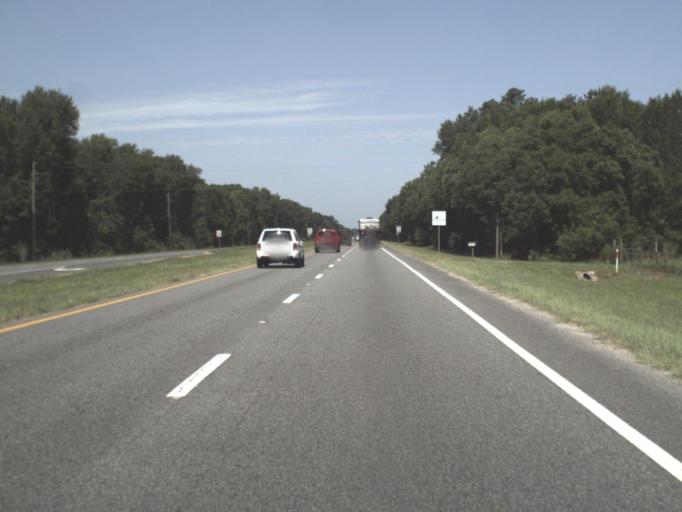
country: US
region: Florida
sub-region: Levy County
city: Manatee Road
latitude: 29.6021
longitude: -82.9914
